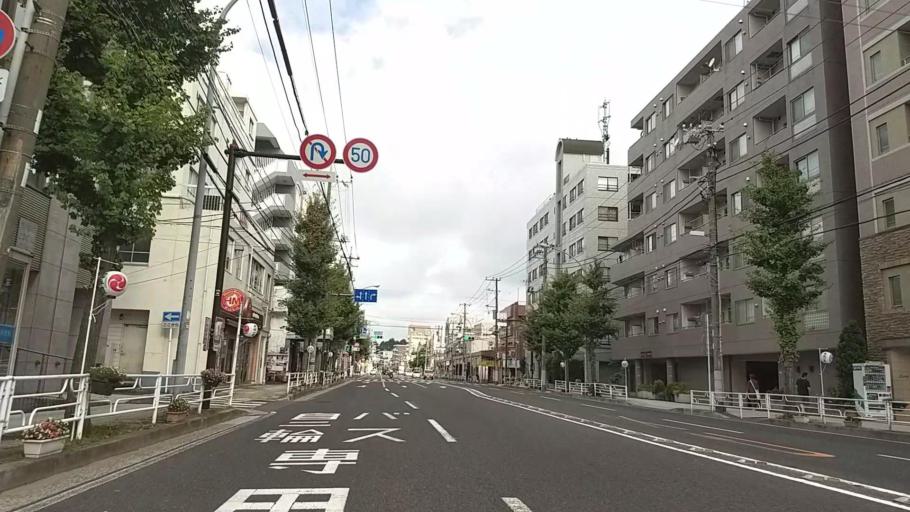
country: JP
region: Kanagawa
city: Yokohama
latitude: 35.4306
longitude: 139.6601
